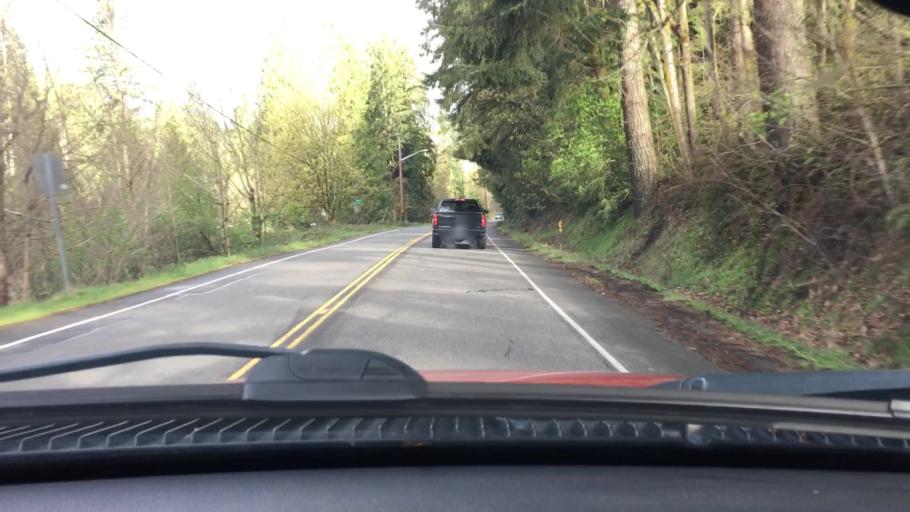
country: US
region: Washington
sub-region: King County
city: Maple Valley
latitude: 47.3716
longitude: -122.0465
